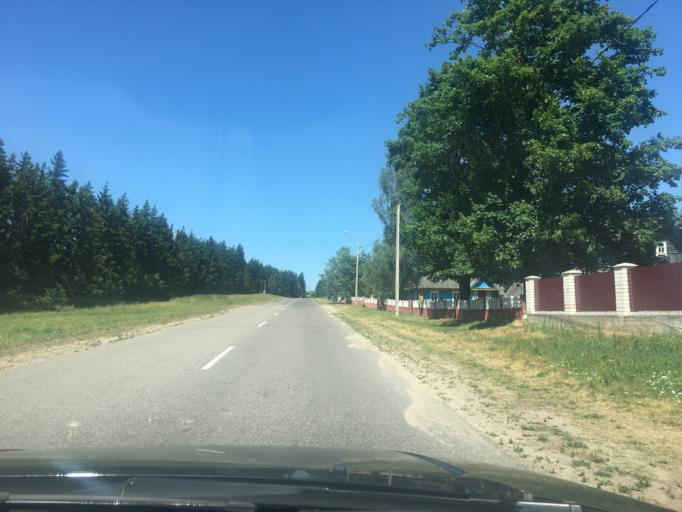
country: BY
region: Grodnenskaya
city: Hal'shany
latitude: 54.2627
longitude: 25.9949
